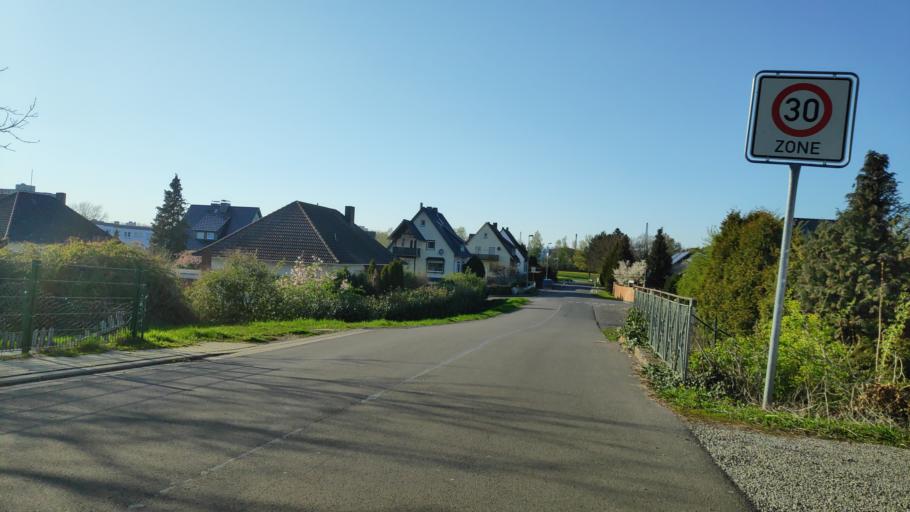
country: DE
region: North Rhine-Westphalia
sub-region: Regierungsbezirk Detmold
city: Minden
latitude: 52.2949
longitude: 8.9543
